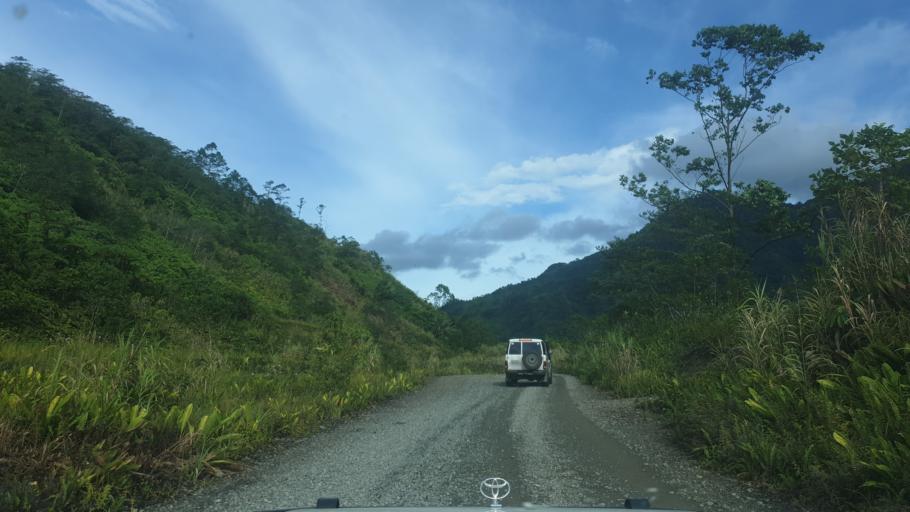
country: PG
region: Bougainville
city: Panguna
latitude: -6.3196
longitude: 155.4816
